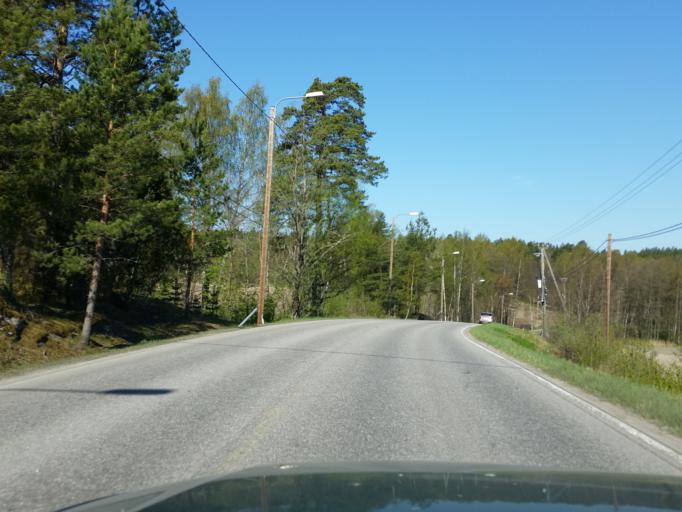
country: FI
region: Uusimaa
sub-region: Helsinki
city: Kirkkonummi
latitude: 60.1537
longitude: 24.4042
